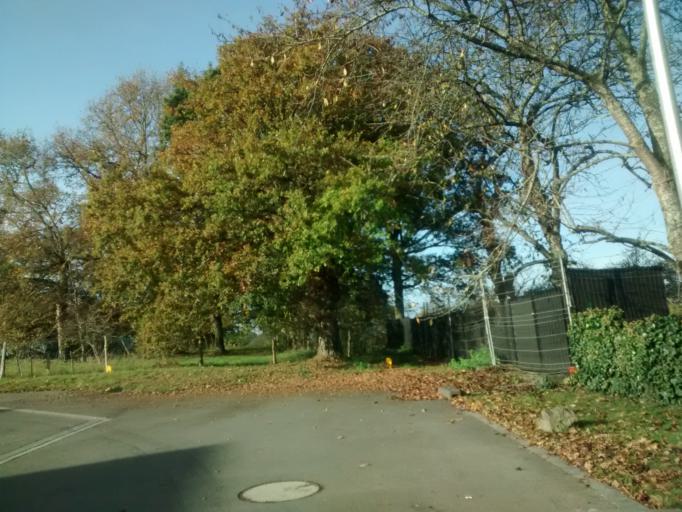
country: FR
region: Brittany
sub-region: Departement d'Ille-et-Vilaine
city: Chantepie
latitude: 48.0990
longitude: -1.6038
